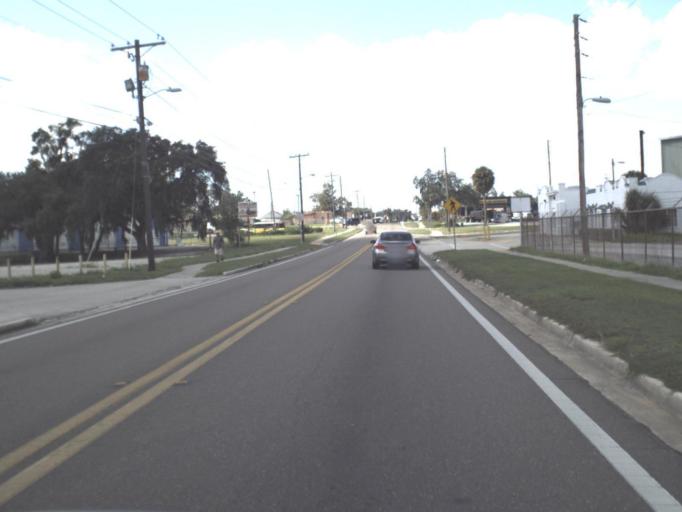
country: US
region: Florida
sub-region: Polk County
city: Davenport
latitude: 28.1634
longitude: -81.6005
